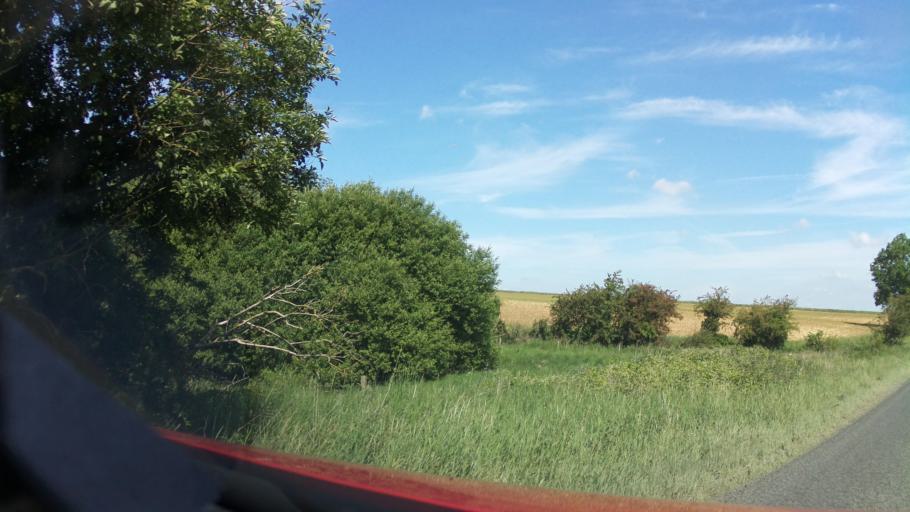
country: GB
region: England
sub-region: North Lincolnshire
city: Redbourne
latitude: 53.4438
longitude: -0.5508
